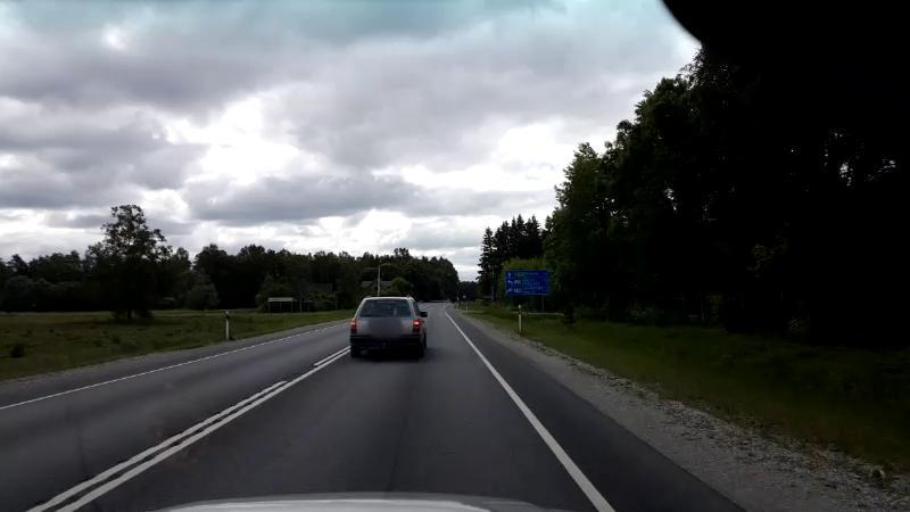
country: EE
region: Paernumaa
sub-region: Halinga vald
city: Parnu-Jaagupi
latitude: 58.6580
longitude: 24.4721
